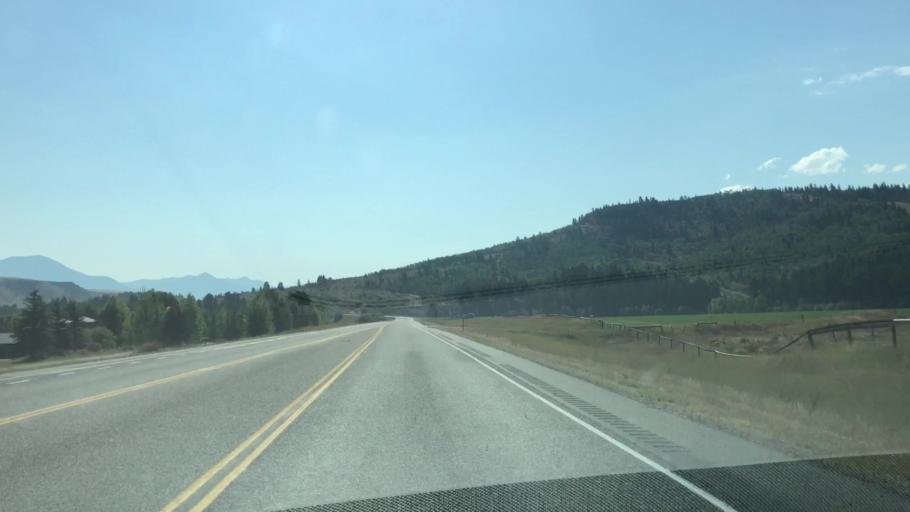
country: US
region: Idaho
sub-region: Teton County
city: Victor
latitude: 43.4610
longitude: -111.4281
